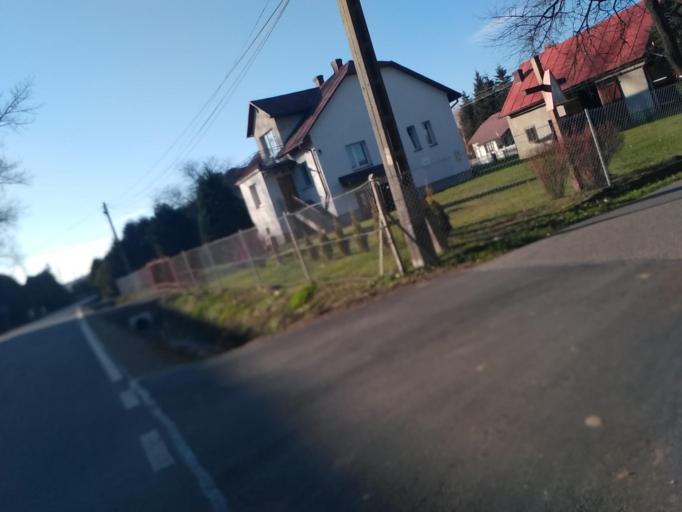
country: PL
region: Subcarpathian Voivodeship
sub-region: Powiat brzozowski
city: Humniska
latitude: 49.6727
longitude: 22.0501
